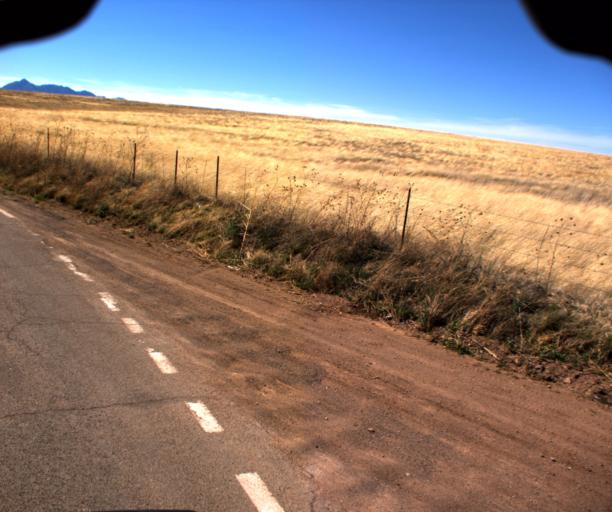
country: US
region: Arizona
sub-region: Cochise County
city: Huachuca City
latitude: 31.6080
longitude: -110.5788
